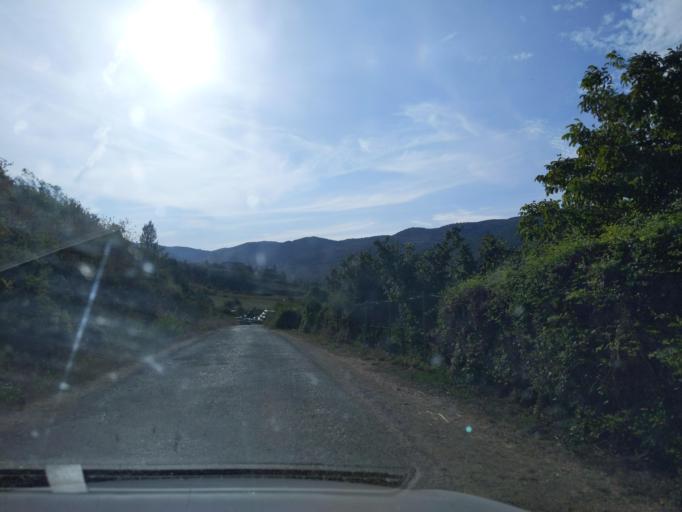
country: ES
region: La Rioja
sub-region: Provincia de La Rioja
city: Ezcaray
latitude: 42.3233
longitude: -3.0224
